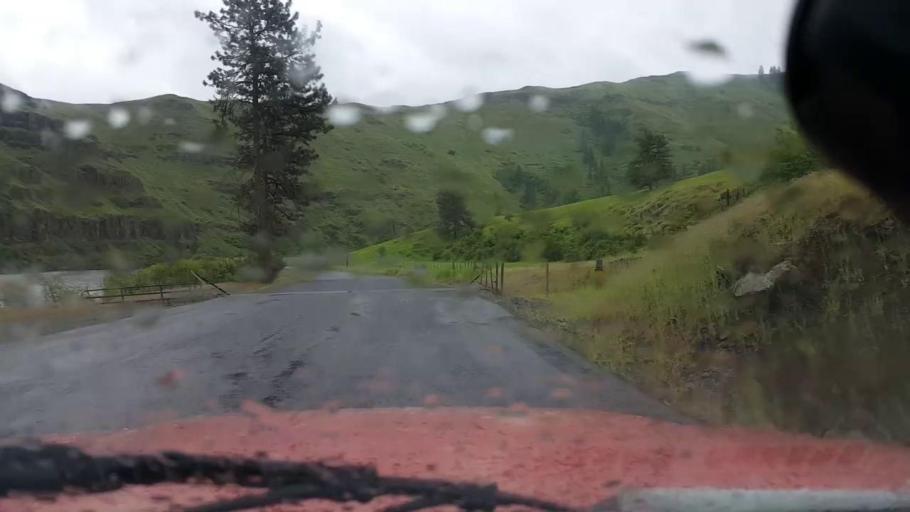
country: US
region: Washington
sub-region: Asotin County
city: Asotin
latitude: 46.0305
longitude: -117.3276
